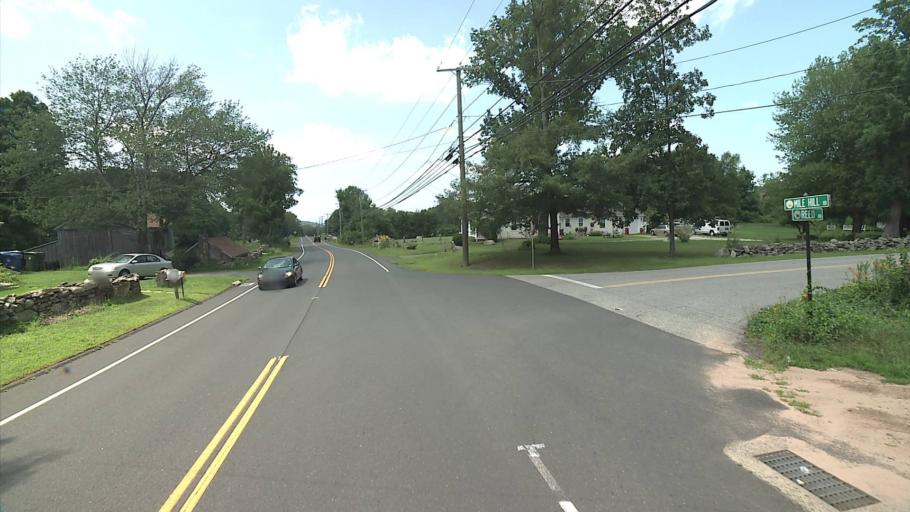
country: US
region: Connecticut
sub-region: Tolland County
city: Rockville
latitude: 41.8428
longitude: -72.4173
